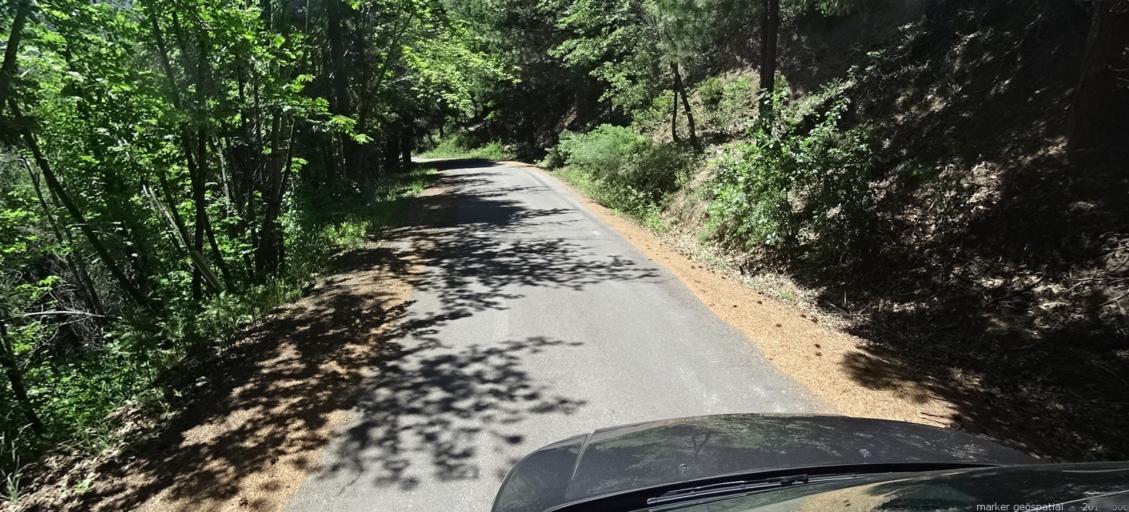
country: US
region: California
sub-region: Siskiyou County
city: Mount Shasta
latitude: 41.2726
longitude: -122.3008
